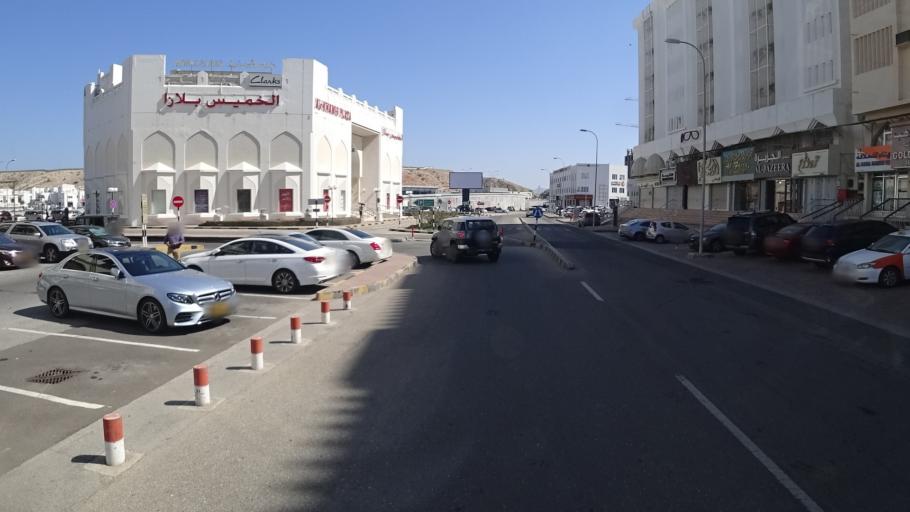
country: OM
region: Muhafazat Masqat
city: Muscat
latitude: 23.6121
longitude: 58.4958
